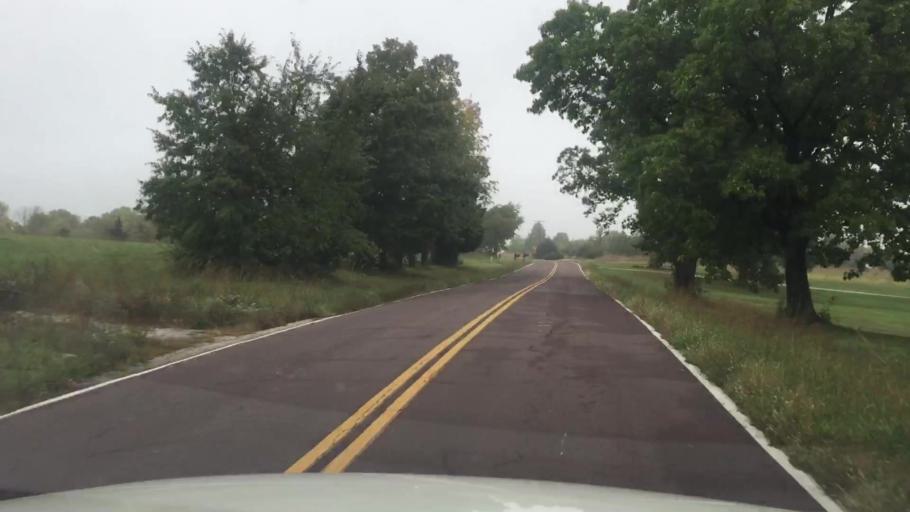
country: US
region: Missouri
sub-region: Boone County
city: Columbia
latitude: 38.8512
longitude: -92.3332
